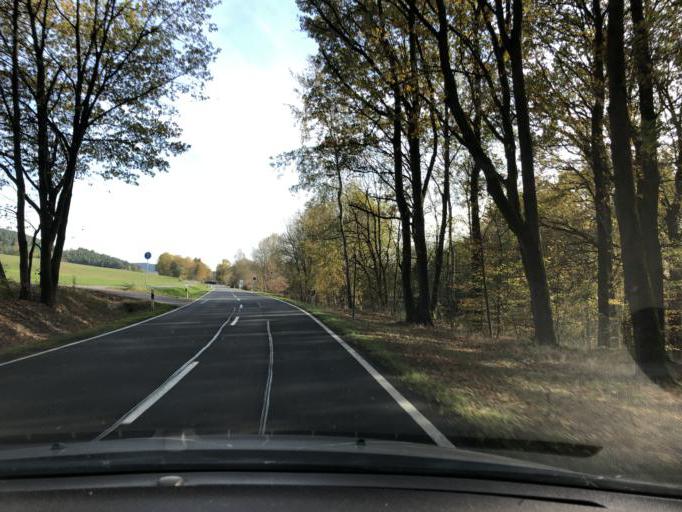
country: DE
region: Thuringia
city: Schleusingen
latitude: 50.4952
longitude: 10.7817
